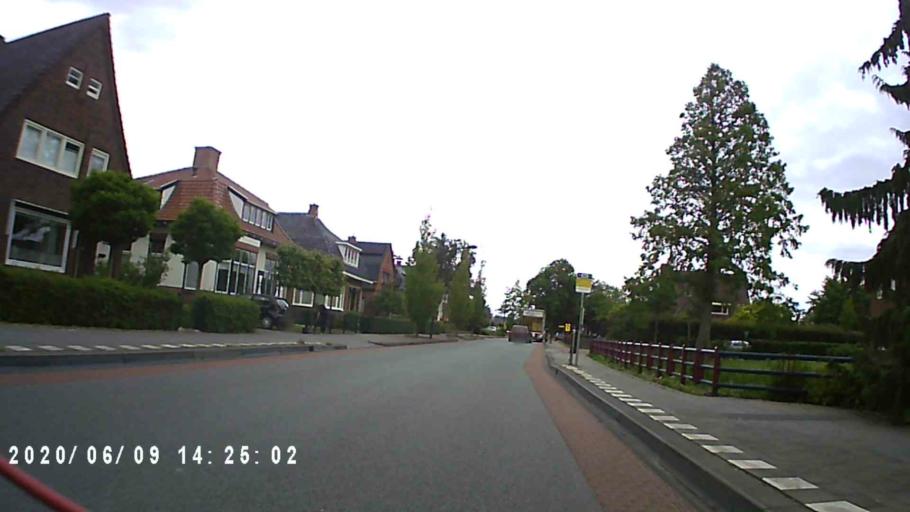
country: NL
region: Groningen
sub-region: Gemeente Bedum
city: Bedum
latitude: 53.3034
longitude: 6.5958
